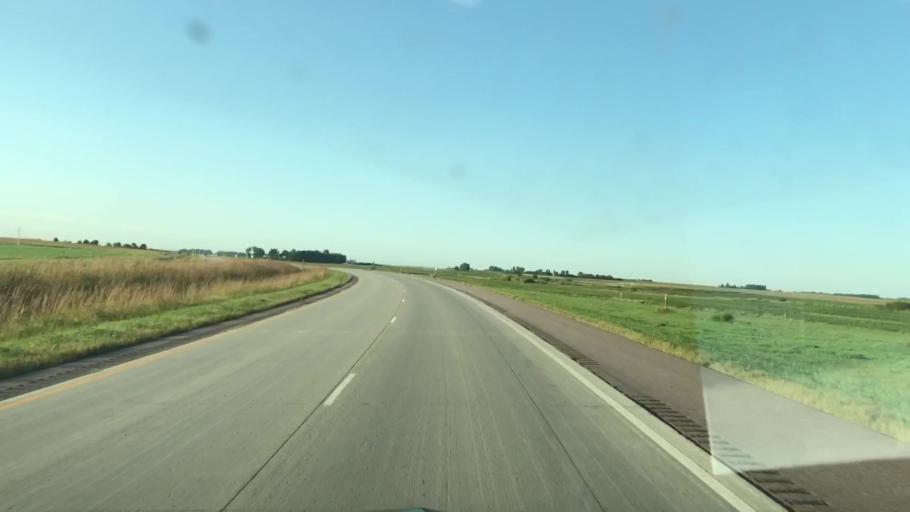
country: US
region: Minnesota
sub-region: Nobles County
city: Worthington
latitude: 43.5766
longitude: -95.6531
